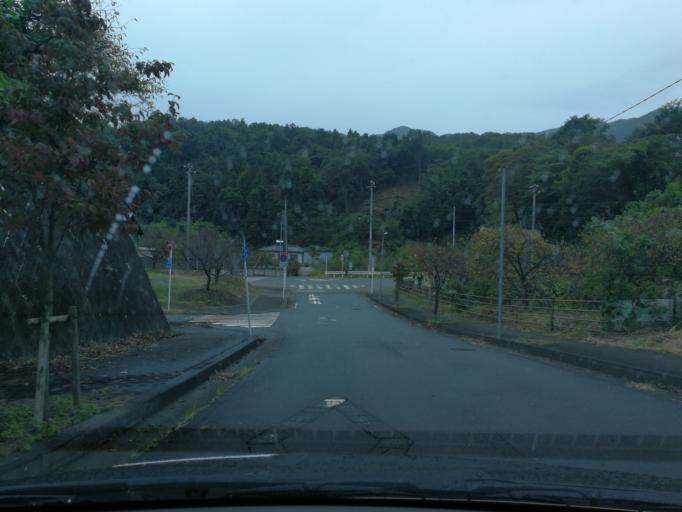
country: JP
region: Yamanashi
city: Uenohara
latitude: 35.6005
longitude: 139.2106
